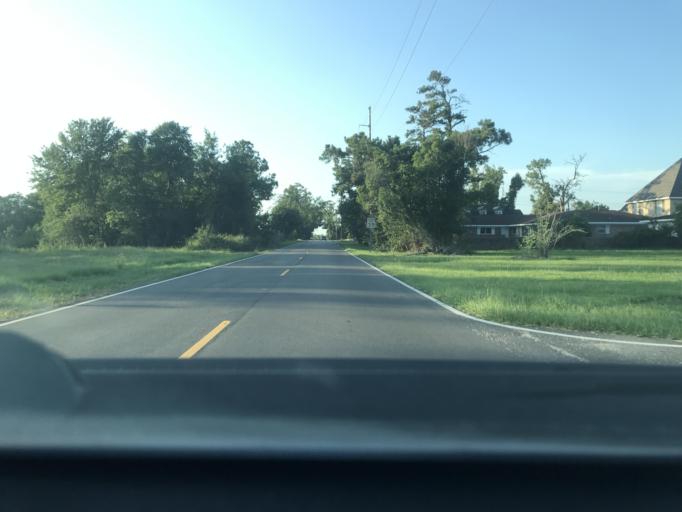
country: US
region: Louisiana
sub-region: Calcasieu Parish
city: Moss Bluff
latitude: 30.2604
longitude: -93.1954
